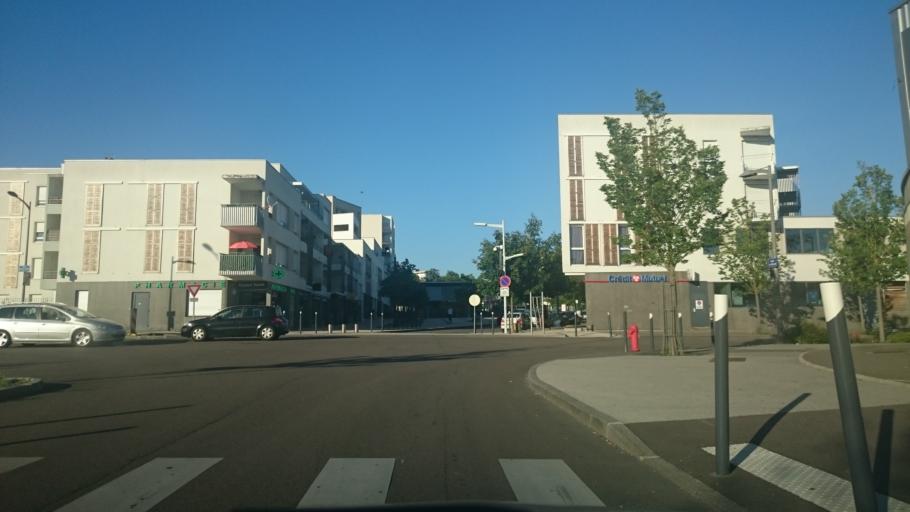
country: FR
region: Bourgogne
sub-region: Departement de la Cote-d'Or
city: Saint-Apollinaire
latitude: 47.3317
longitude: 5.0663
